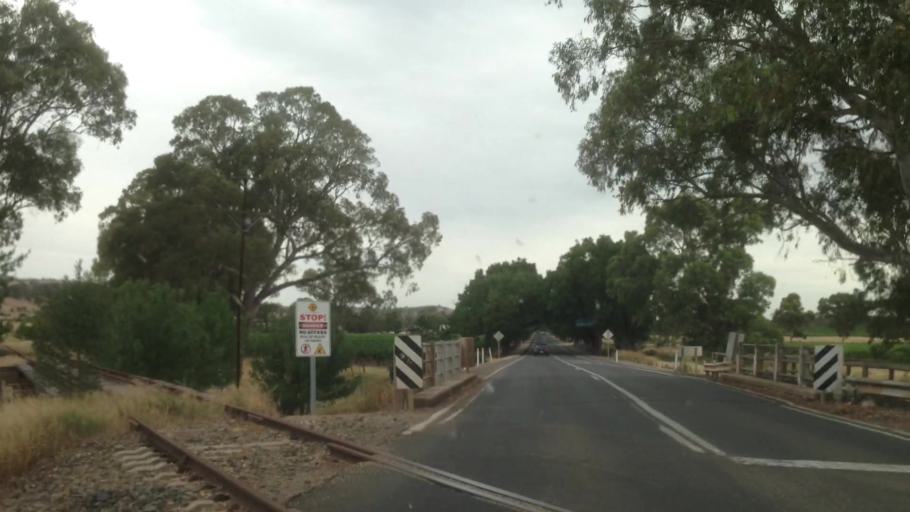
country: AU
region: South Australia
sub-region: Barossa
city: Lyndoch
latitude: -34.6061
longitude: 138.8919
